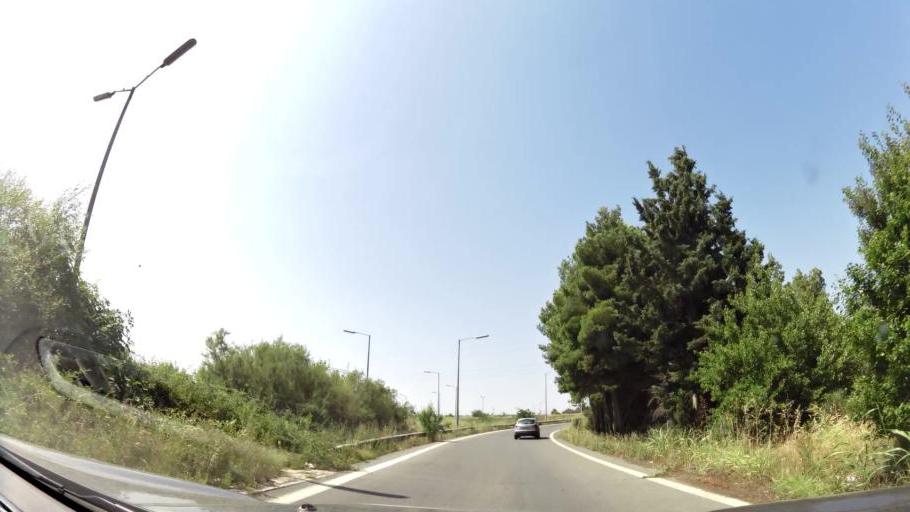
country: GR
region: Central Macedonia
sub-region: Nomos Thessalonikis
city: Agios Athanasios
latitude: 40.7218
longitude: 22.7136
